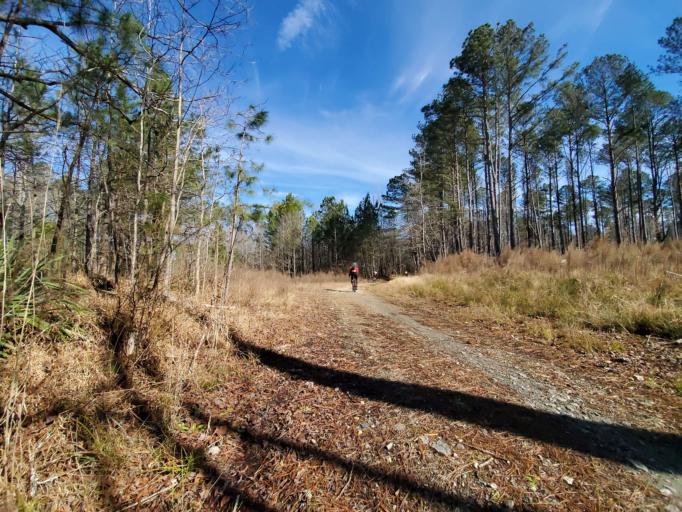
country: US
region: Georgia
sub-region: Fulton County
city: Chattahoochee Hills
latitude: 33.5696
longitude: -84.7380
